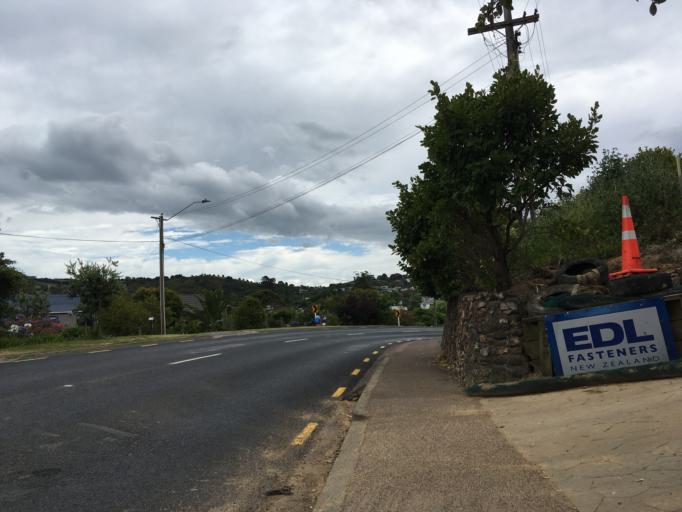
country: NZ
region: Auckland
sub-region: Auckland
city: Pakuranga
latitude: -36.7848
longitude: 175.0141
